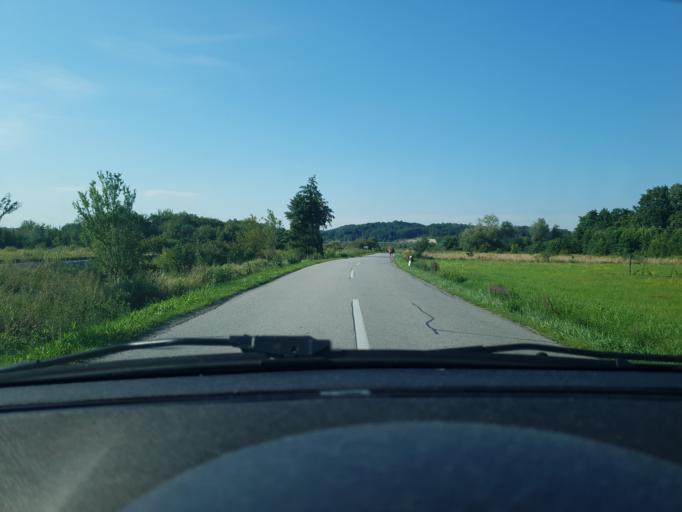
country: HR
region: Krapinsko-Zagorska
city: Oroslavje
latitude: 46.0071
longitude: 15.9308
